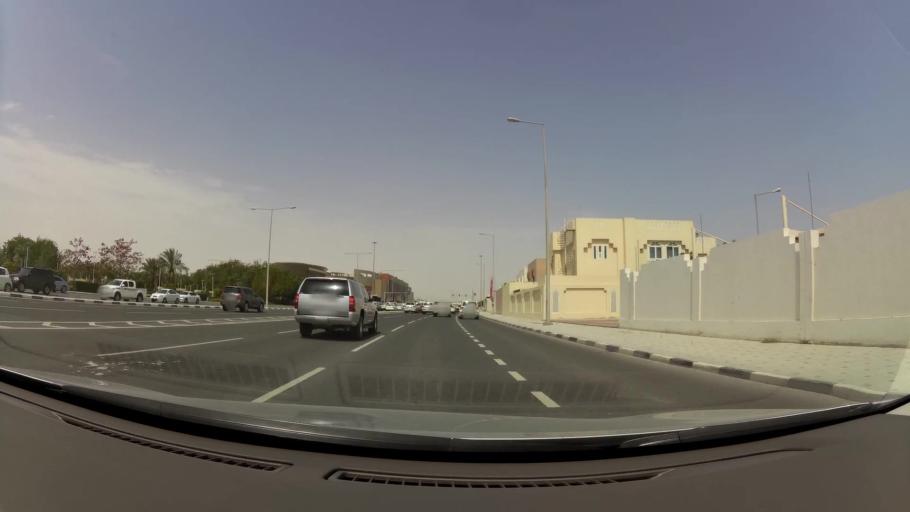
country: QA
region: Baladiyat ad Dawhah
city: Doha
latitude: 25.3332
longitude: 51.4821
